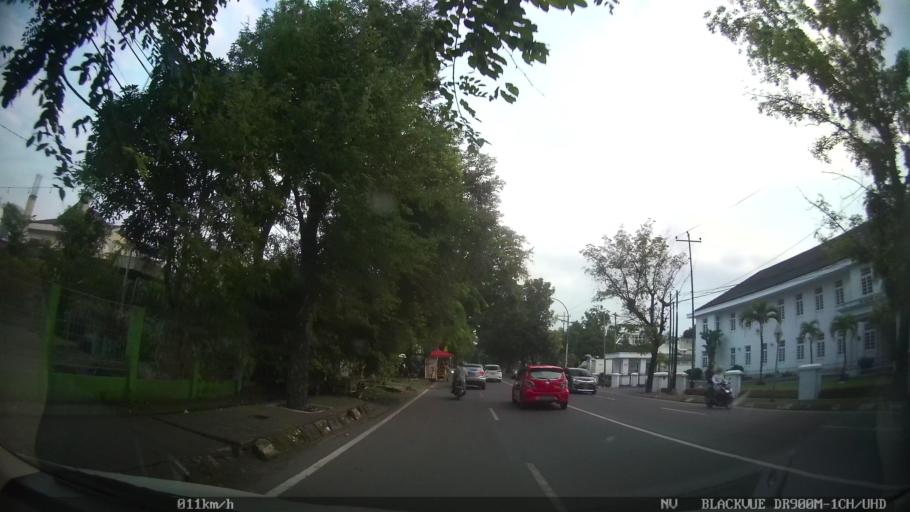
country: ID
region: North Sumatra
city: Medan
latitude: 3.5998
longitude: 98.6691
